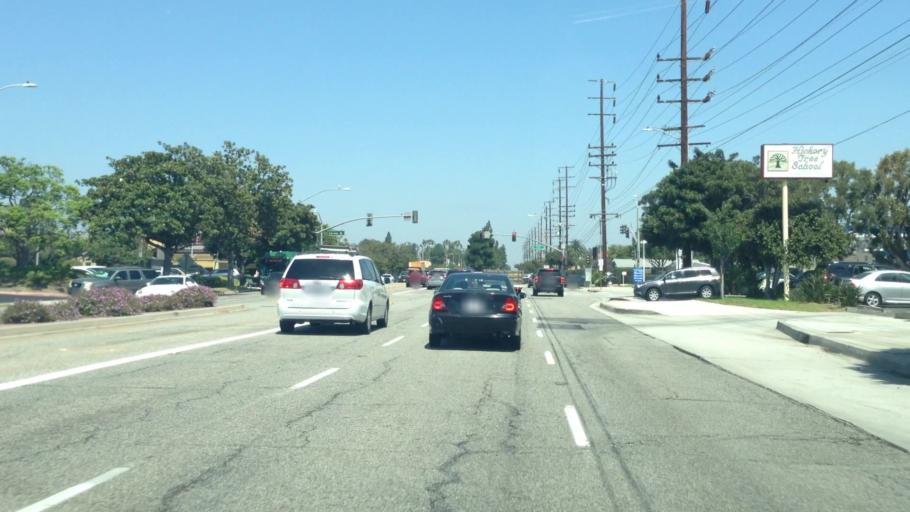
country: US
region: California
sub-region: Los Angeles County
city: Torrance
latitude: 33.8299
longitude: -118.3449
